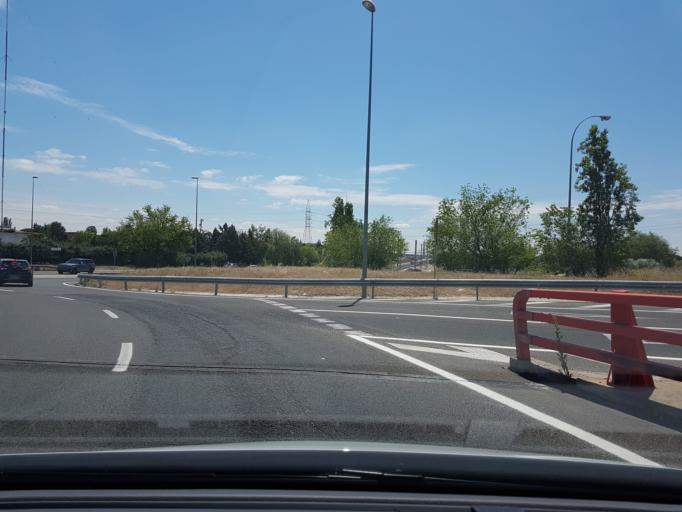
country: ES
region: Madrid
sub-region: Provincia de Madrid
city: Pozuelo de Alarcon
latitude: 40.4287
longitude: -3.8111
